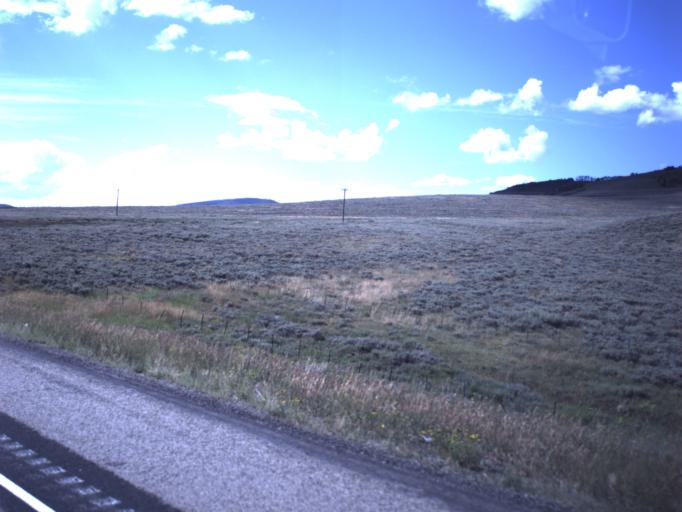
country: US
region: Utah
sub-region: Wasatch County
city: Heber
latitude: 40.2368
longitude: -111.1359
